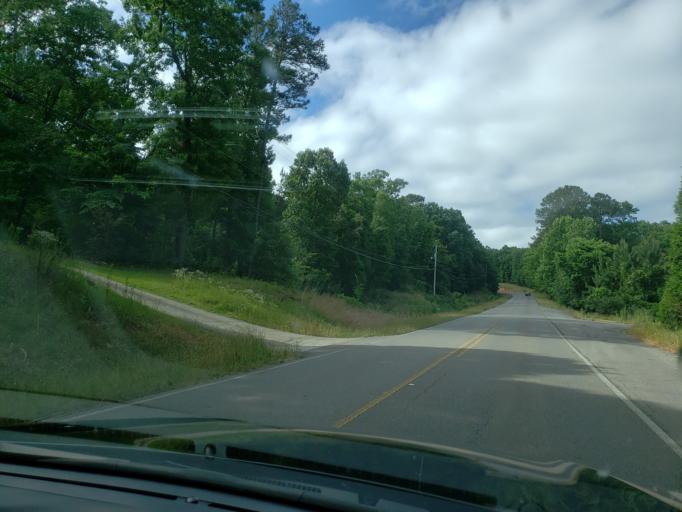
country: US
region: Alabama
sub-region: Calhoun County
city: Saks
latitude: 33.7333
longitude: -85.8484
